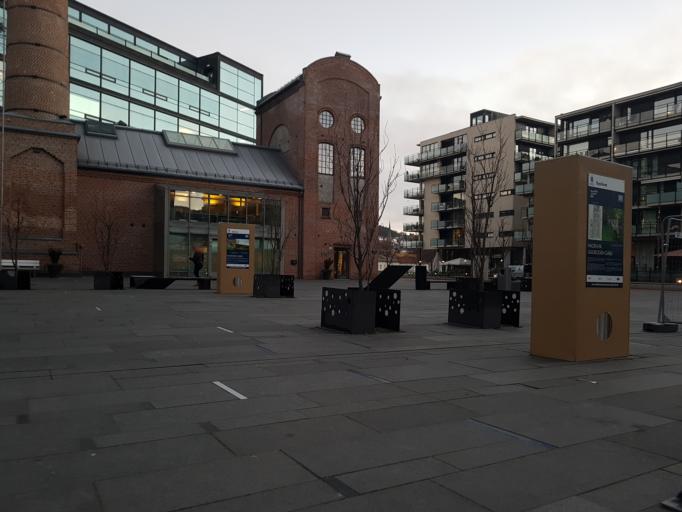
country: NO
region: Buskerud
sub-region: Drammen
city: Drammen
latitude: 59.7433
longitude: 10.1935
